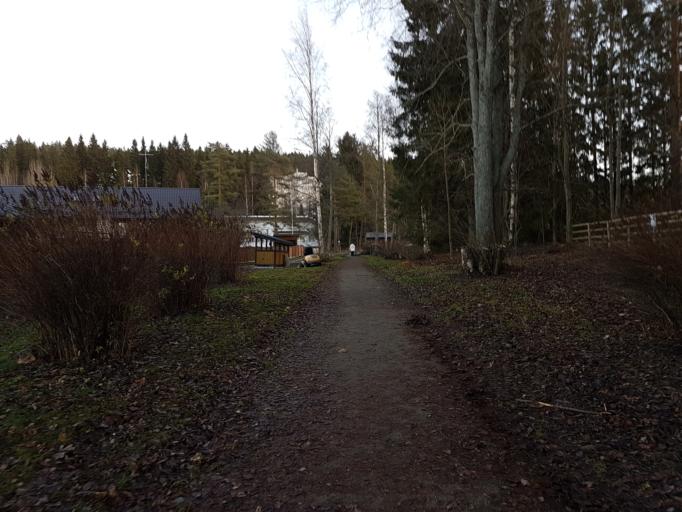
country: FI
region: Northern Savo
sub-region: Kuopio
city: Kuopio
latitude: 62.9340
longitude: 27.6302
